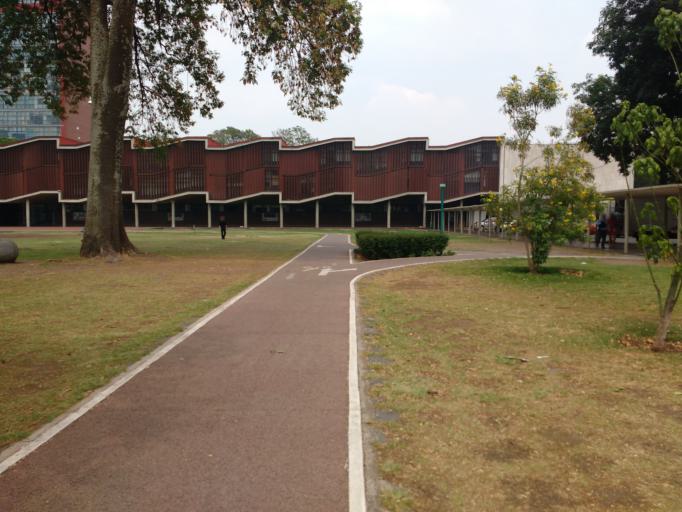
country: MX
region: Mexico City
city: Coyoacan
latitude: 19.3324
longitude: -99.1842
